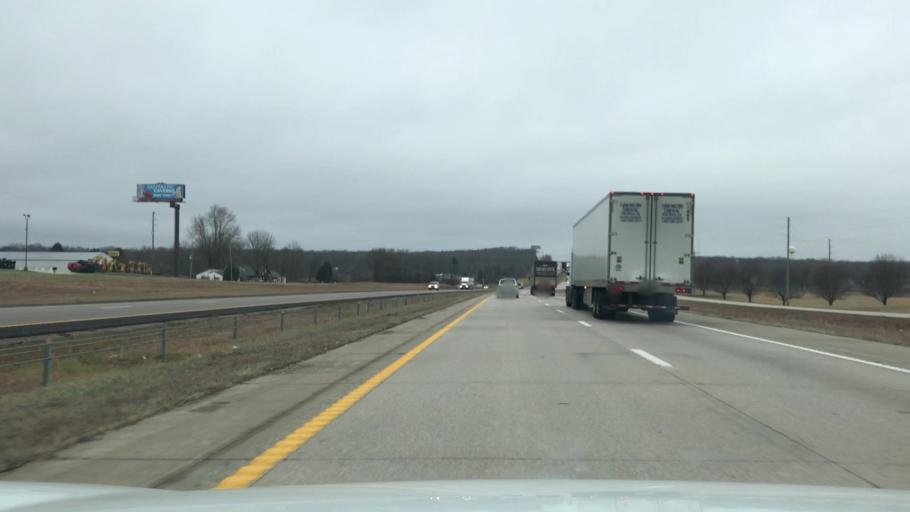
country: US
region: Missouri
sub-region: Franklin County
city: Sullivan
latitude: 38.1926
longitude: -91.1884
